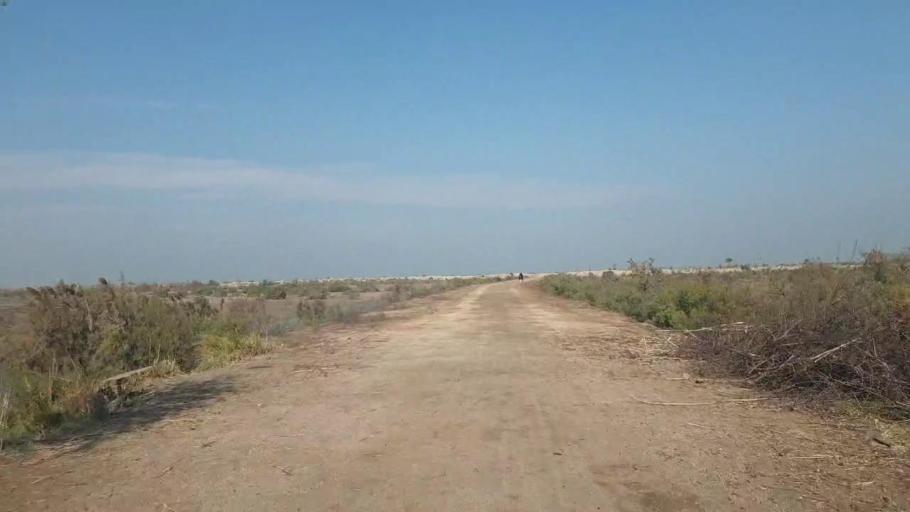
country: PK
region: Sindh
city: Shahdadpur
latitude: 25.9741
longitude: 68.5101
